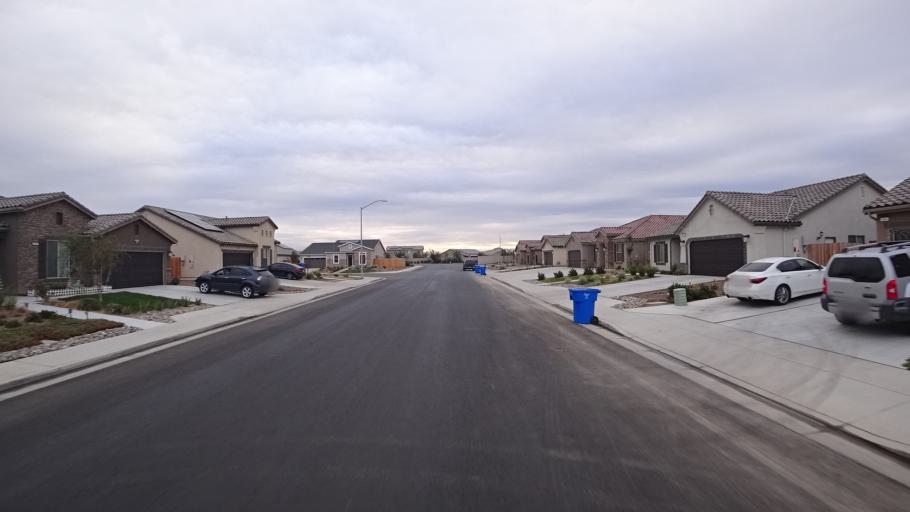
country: US
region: California
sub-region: Kern County
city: Greenfield
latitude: 35.2934
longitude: -119.0669
